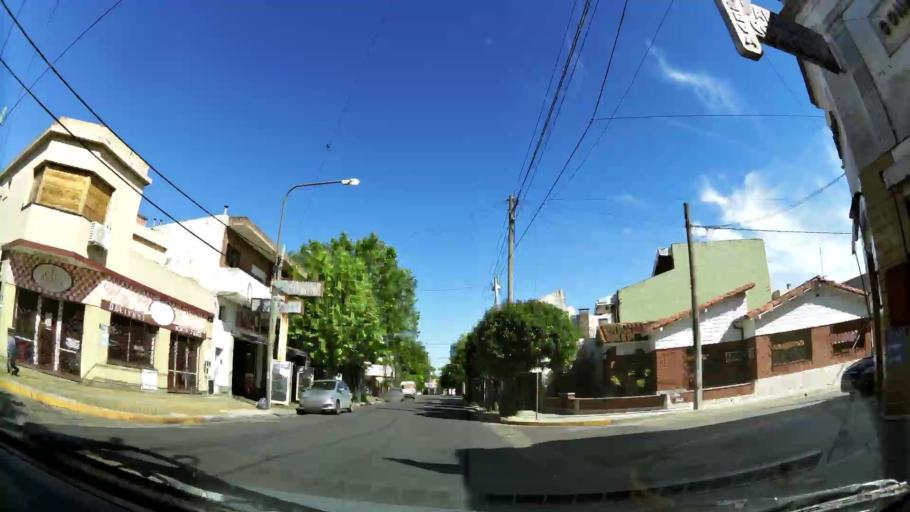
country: AR
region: Buenos Aires
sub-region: Partido de Quilmes
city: Quilmes
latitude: -34.7042
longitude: -58.2890
